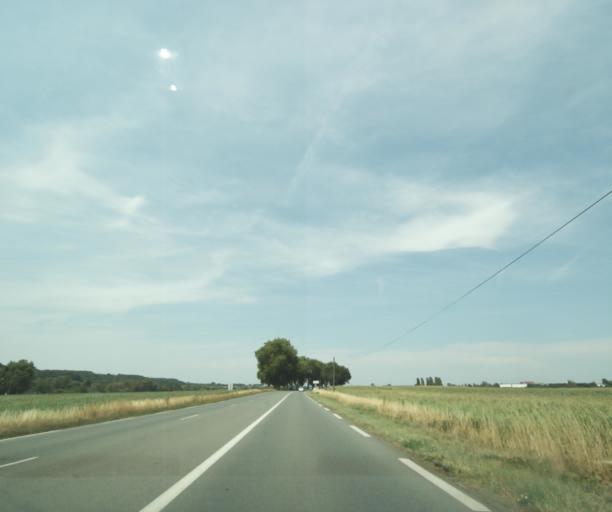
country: FR
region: Poitou-Charentes
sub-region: Departement de la Vienne
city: Antran
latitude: 46.8928
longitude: 0.5693
